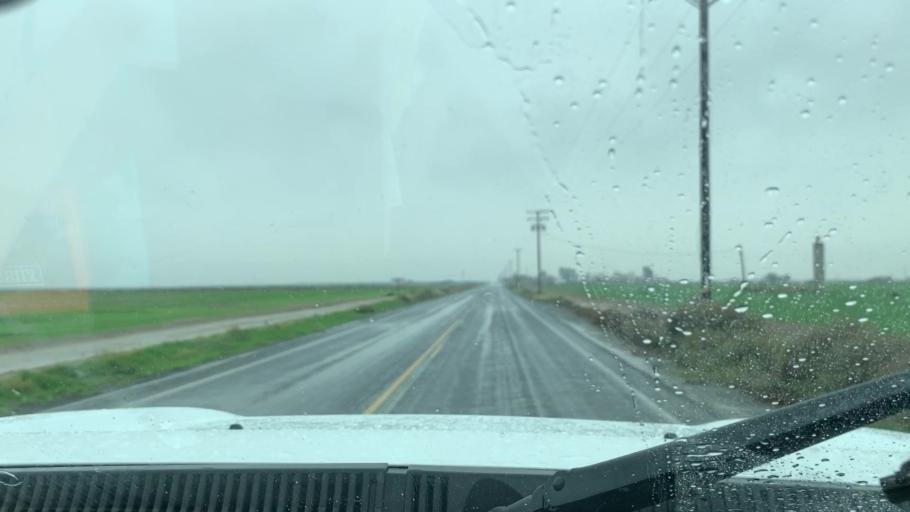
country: US
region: California
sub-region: Tulare County
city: Earlimart
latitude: 35.8919
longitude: -119.3048
